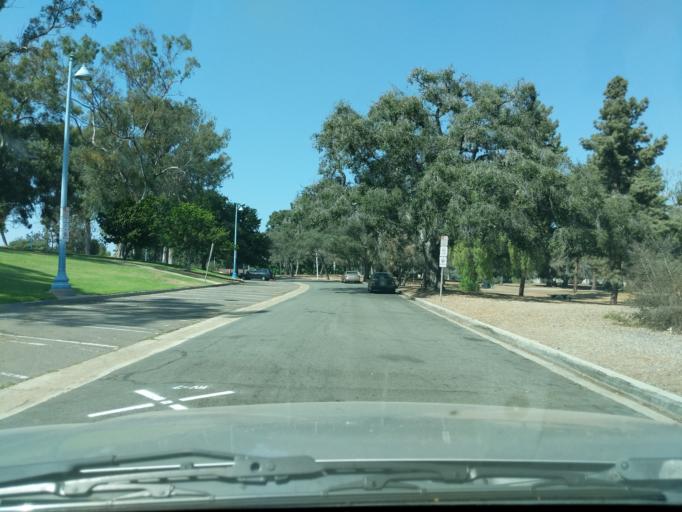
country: US
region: California
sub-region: San Diego County
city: San Diego
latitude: 32.7278
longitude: -117.1576
